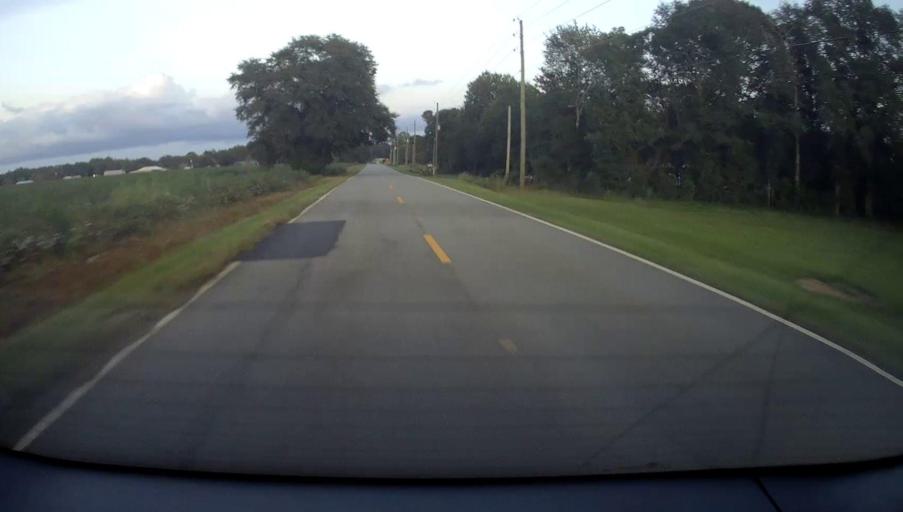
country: US
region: Georgia
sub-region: Houston County
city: Centerville
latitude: 32.6433
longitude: -83.7045
